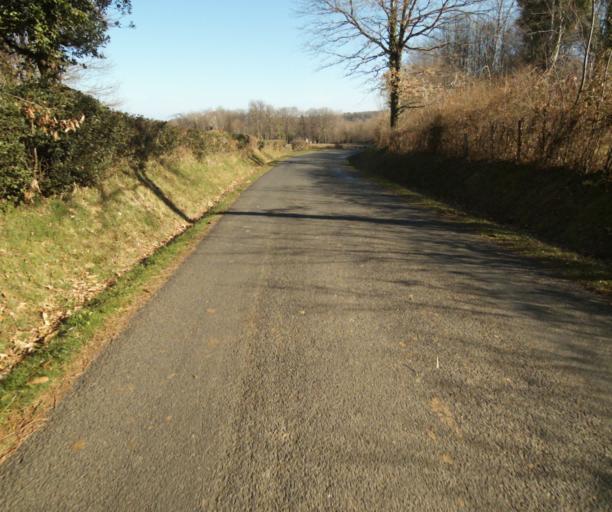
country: FR
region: Limousin
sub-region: Departement de la Correze
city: Saint-Clement
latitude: 45.3764
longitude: 1.6440
